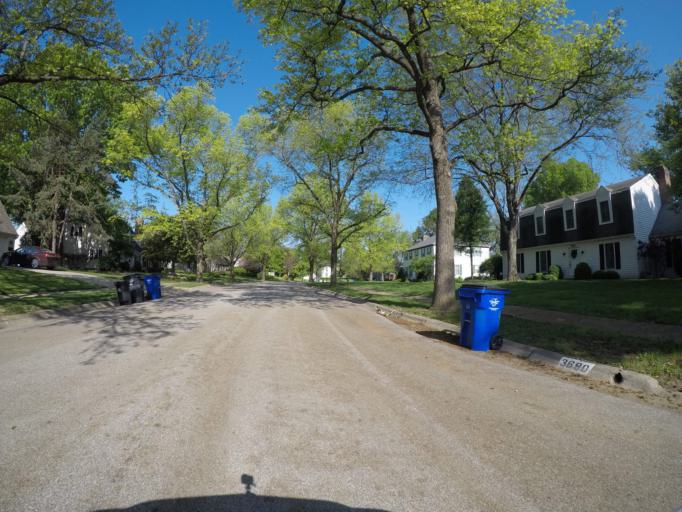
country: US
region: Ohio
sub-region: Franklin County
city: Upper Arlington
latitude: 40.0327
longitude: -83.0481
